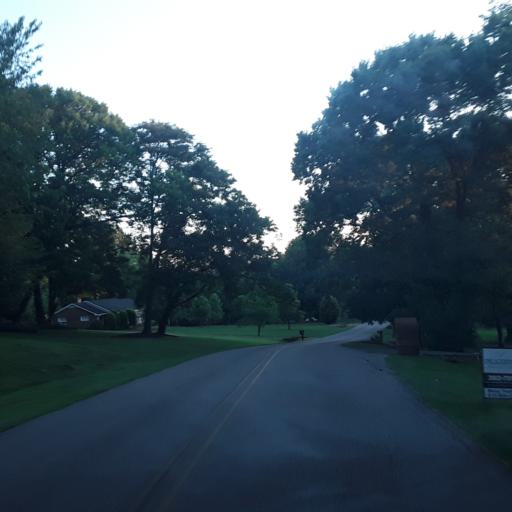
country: US
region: Tennessee
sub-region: Davidson County
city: Oak Hill
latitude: 36.0691
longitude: -86.7716
